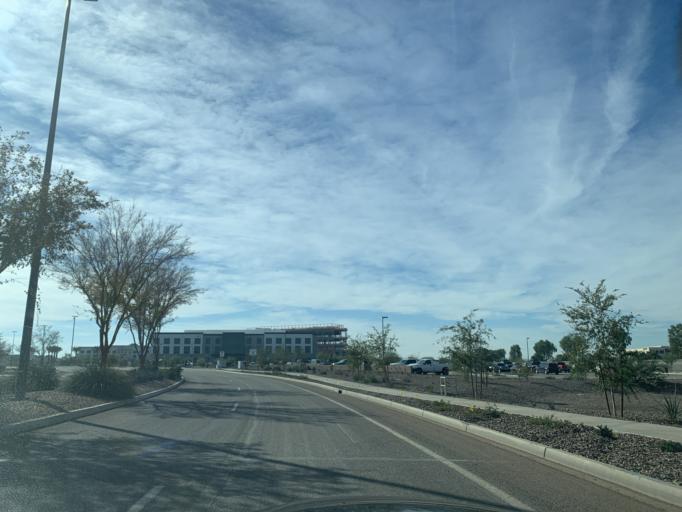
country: US
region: Arizona
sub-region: Maricopa County
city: Gilbert
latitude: 33.2912
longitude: -111.7478
